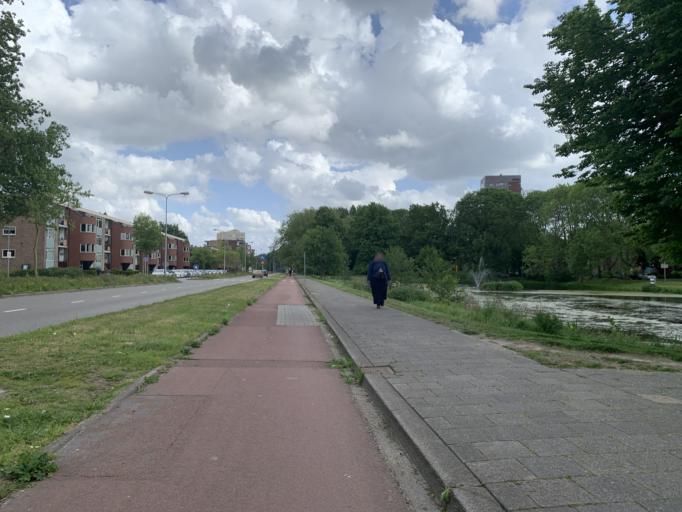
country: NL
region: Groningen
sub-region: Gemeente Groningen
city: Groningen
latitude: 53.2282
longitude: 6.5432
